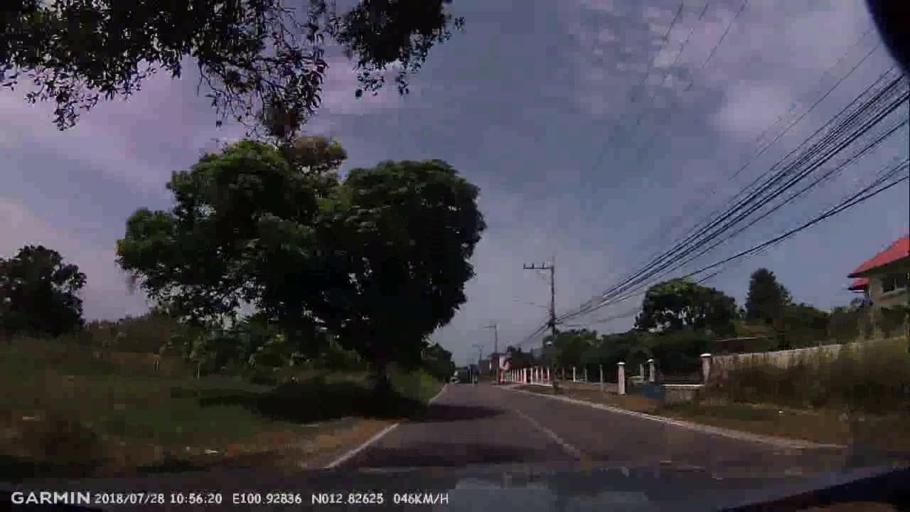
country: TH
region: Chon Buri
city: Phatthaya
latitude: 12.8261
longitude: 100.9282
